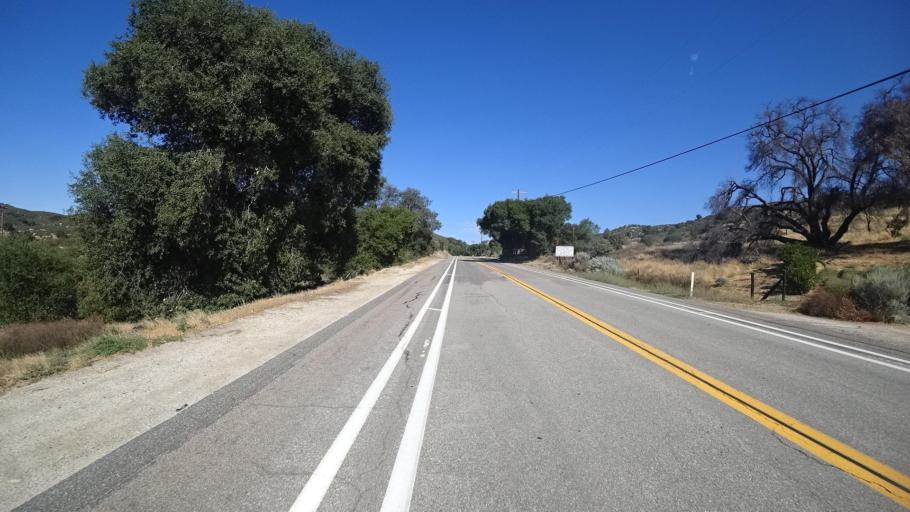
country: US
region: California
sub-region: San Diego County
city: Julian
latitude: 33.1956
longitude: -116.5951
